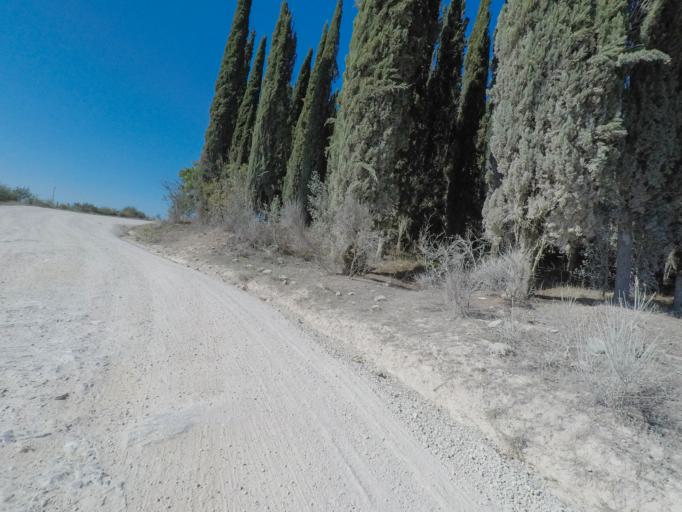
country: IT
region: Tuscany
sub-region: Provincia di Siena
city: Castellina in Chianti
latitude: 43.4353
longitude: 11.3125
